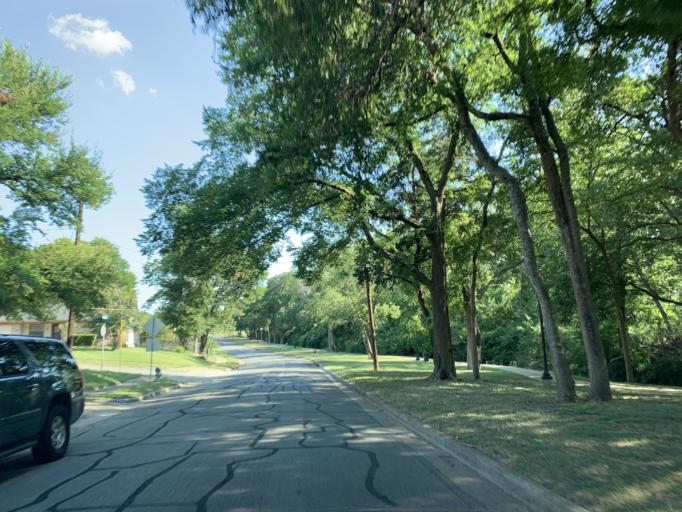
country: US
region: Texas
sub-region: Dallas County
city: Hutchins
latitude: 32.6608
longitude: -96.7753
